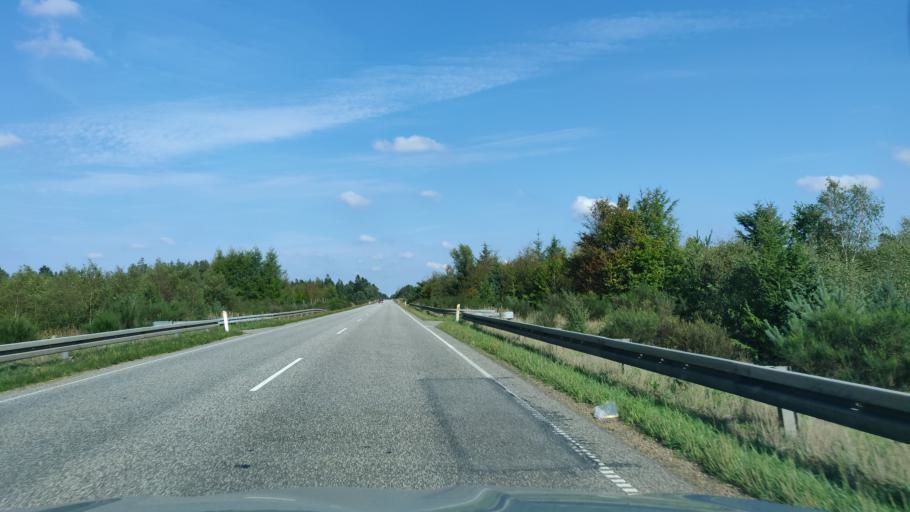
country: DK
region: Central Jutland
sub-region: Herning Kommune
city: Sunds
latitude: 56.3654
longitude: 8.9784
